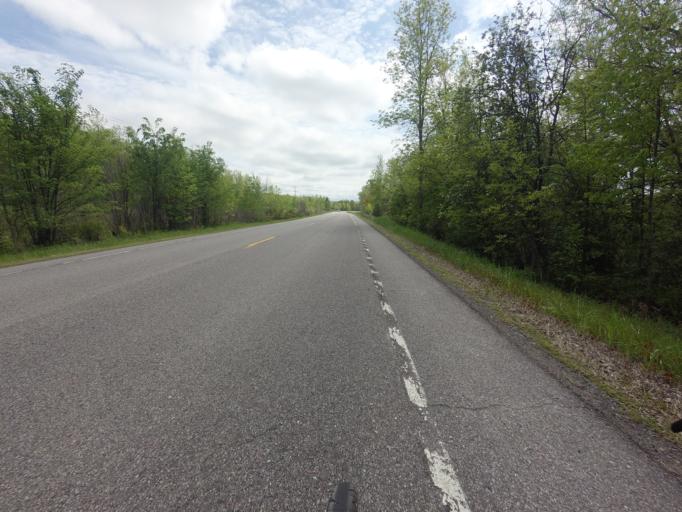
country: CA
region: Ontario
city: Cornwall
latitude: 44.9644
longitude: -74.6656
